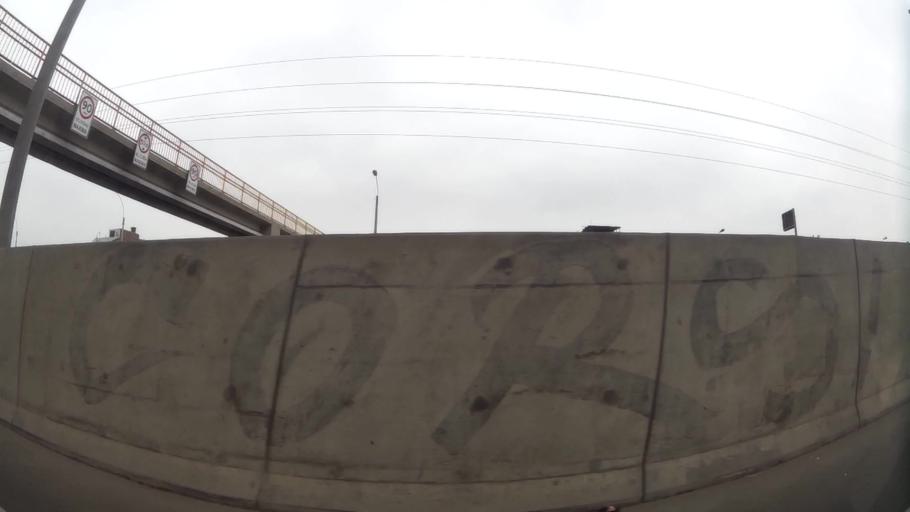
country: PE
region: Lima
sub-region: Lima
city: Independencia
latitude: -11.9741
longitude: -77.0666
